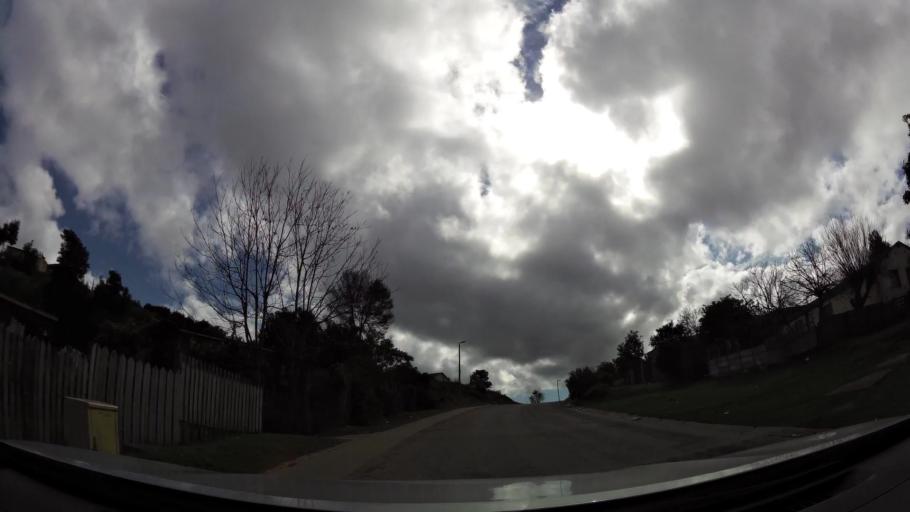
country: ZA
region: Western Cape
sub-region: Eden District Municipality
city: Knysna
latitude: -34.0531
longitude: 23.0960
